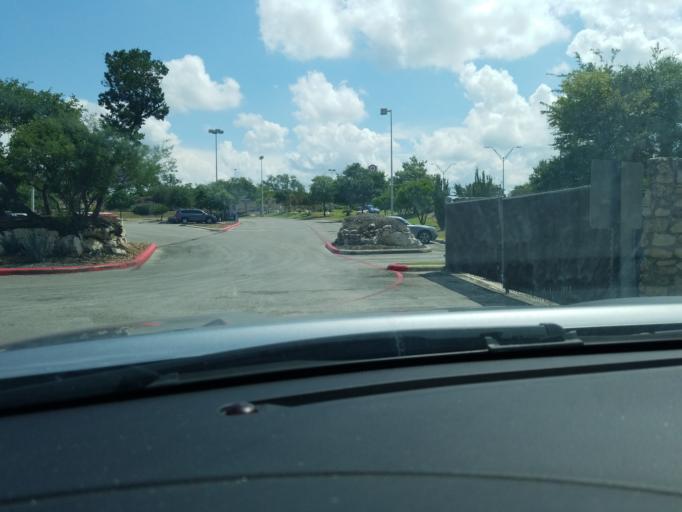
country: US
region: Texas
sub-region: Bexar County
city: Timberwood Park
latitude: 29.6507
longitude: -98.4472
